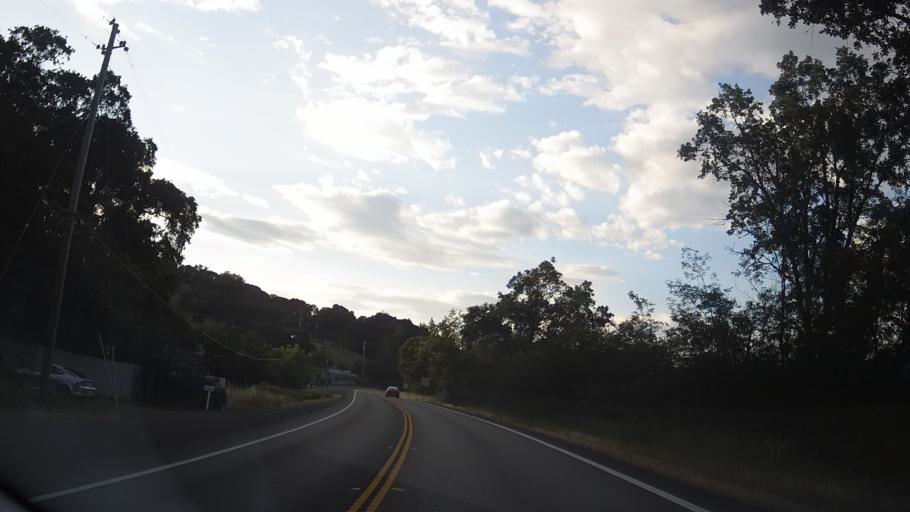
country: US
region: California
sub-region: Mendocino County
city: Talmage
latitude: 38.9782
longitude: -123.1150
